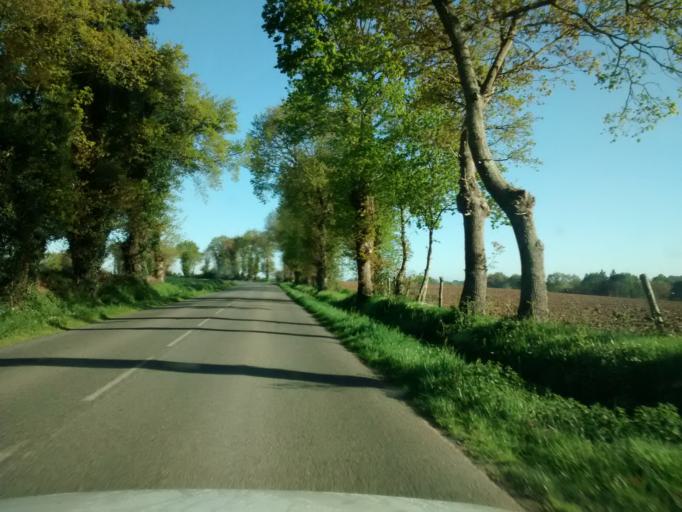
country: FR
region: Brittany
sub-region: Departement du Morbihan
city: Malestroit
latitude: 47.8186
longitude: -2.3989
